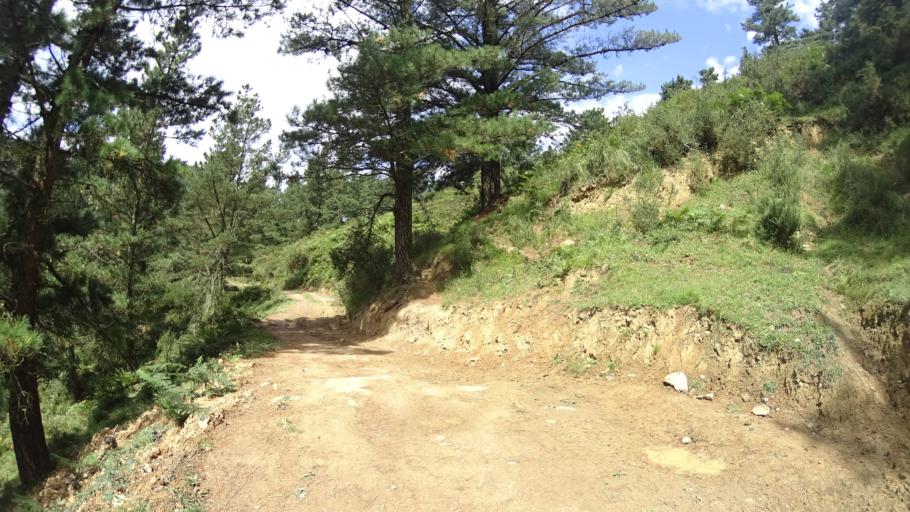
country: ES
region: Basque Country
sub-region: Bizkaia
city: Urtuella
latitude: 43.2827
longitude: -3.0714
